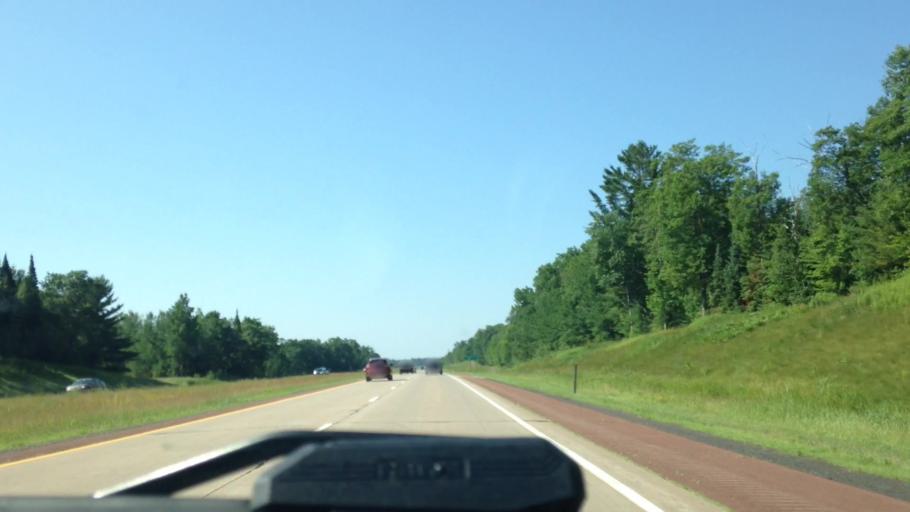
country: US
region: Wisconsin
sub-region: Douglas County
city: Lake Nebagamon
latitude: 46.3784
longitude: -91.8245
